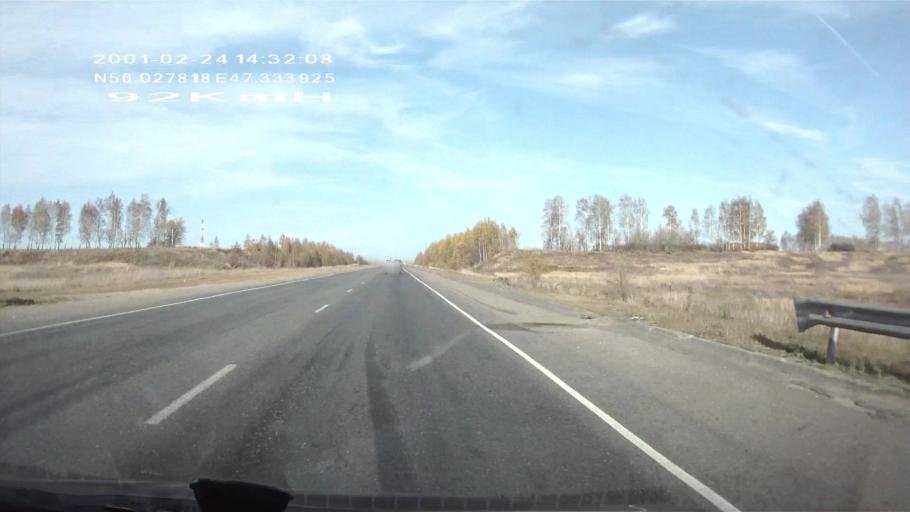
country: RU
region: Chuvashia
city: Kugesi
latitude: 56.0275
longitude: 47.3334
